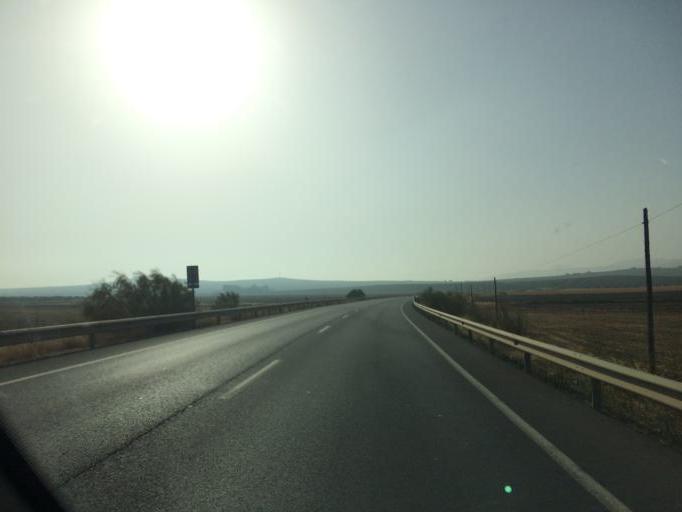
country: ES
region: Andalusia
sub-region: Provincia de Malaga
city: Humilladero
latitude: 37.0629
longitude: -4.7013
